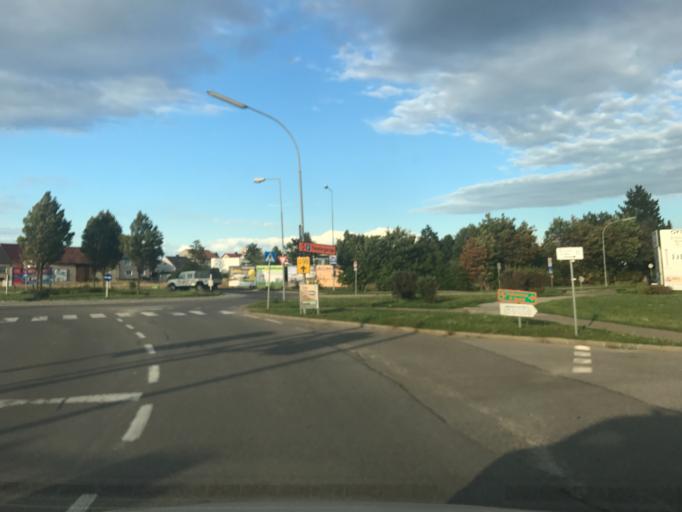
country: AT
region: Lower Austria
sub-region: Wiener Neustadt Stadt
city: Wiener Neustadt
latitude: 47.8099
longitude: 16.2149
